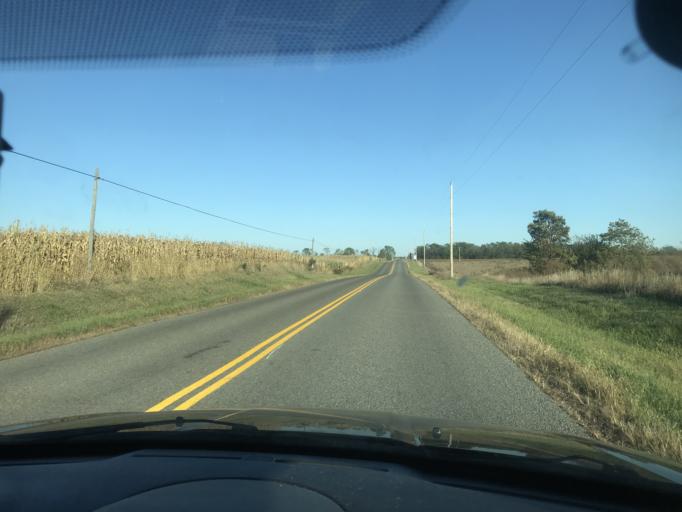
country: US
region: Ohio
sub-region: Logan County
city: Bellefontaine
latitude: 40.3214
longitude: -83.8264
